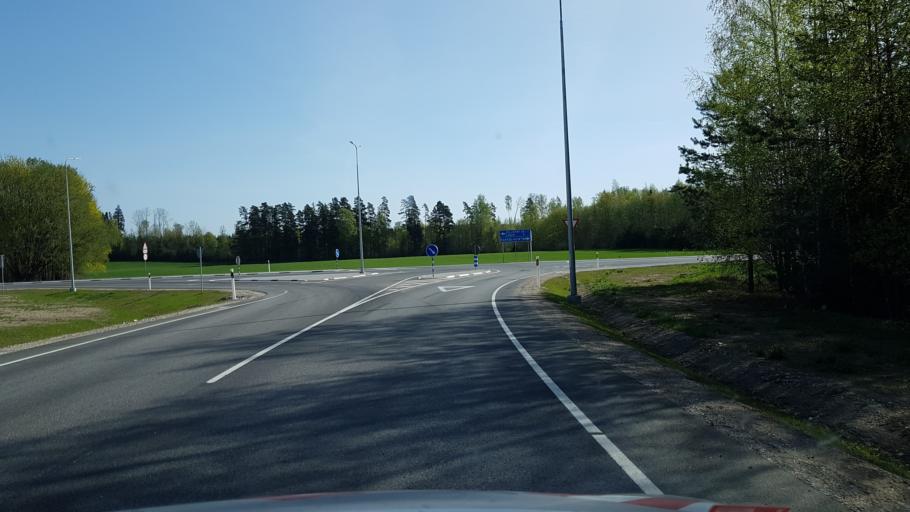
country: EE
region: Viljandimaa
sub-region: Viljandi linn
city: Viljandi
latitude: 58.2408
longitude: 25.5939
